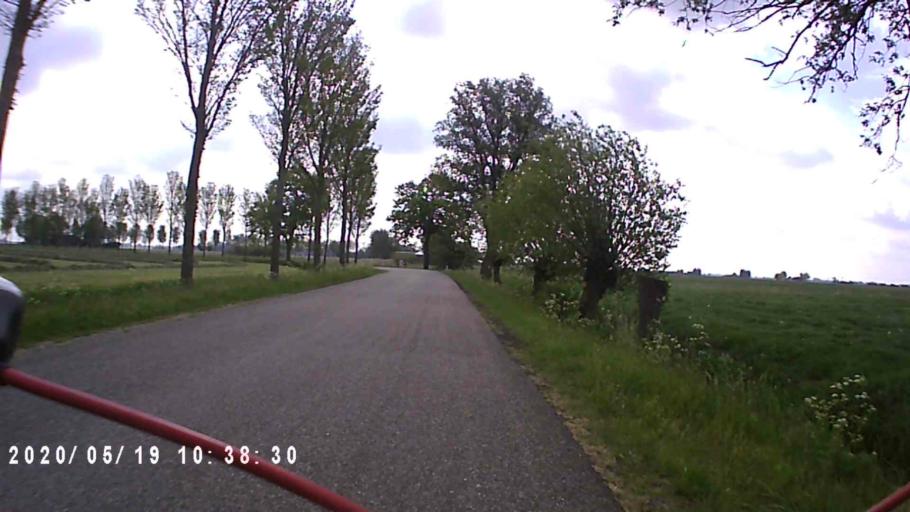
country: NL
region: Friesland
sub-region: Gemeente Kollumerland en Nieuwkruisland
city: Kollum
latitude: 53.2717
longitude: 6.1890
